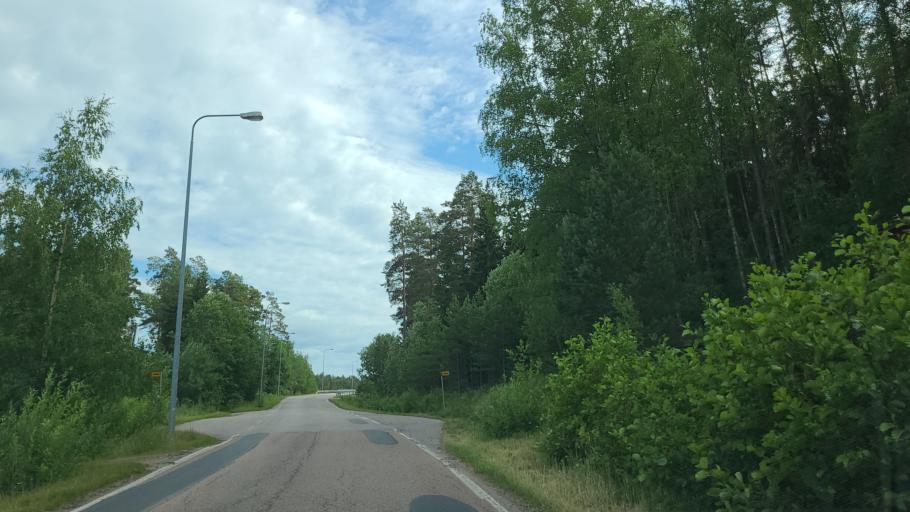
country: FI
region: Varsinais-Suomi
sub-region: Turku
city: Rymaettylae
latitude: 60.3400
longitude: 21.9781
